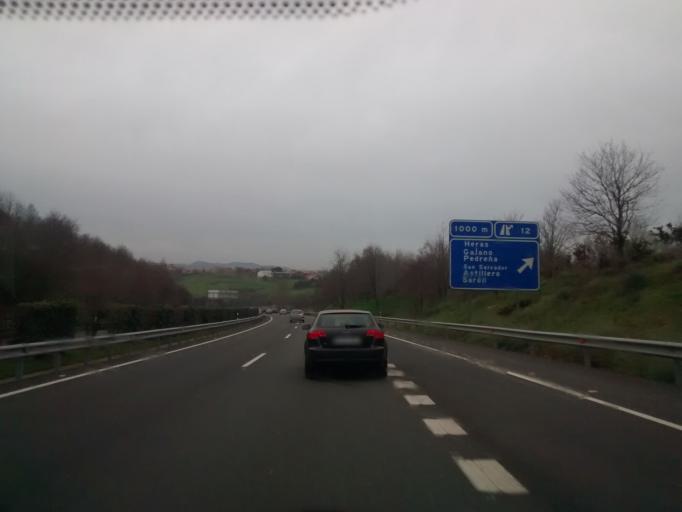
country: ES
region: Cantabria
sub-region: Provincia de Cantabria
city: Lierganes
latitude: 43.3938
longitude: -3.7510
